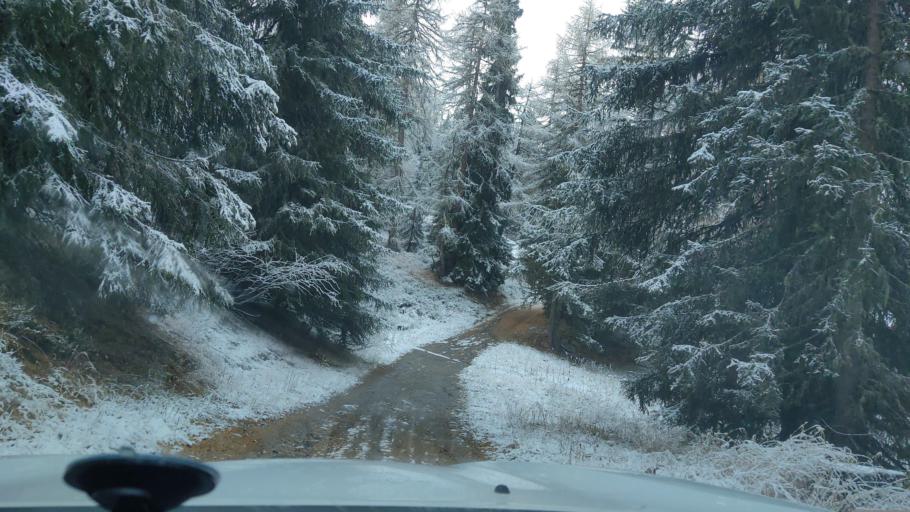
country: FR
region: Rhone-Alpes
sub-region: Departement de la Savoie
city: Seez
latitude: 45.5925
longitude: 6.8052
